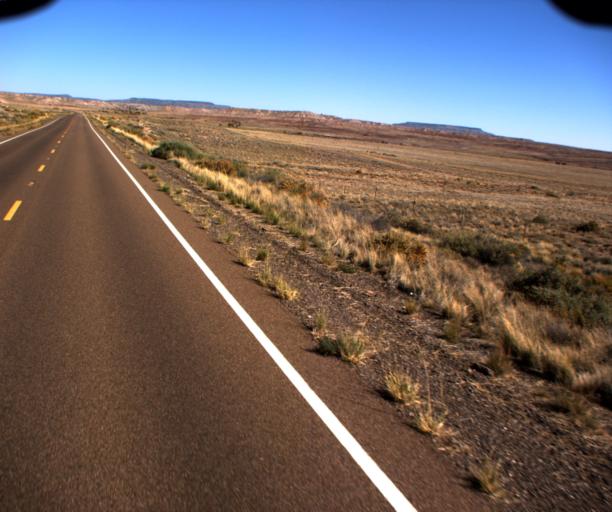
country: US
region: Arizona
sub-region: Navajo County
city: Joseph City
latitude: 35.1644
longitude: -110.4540
